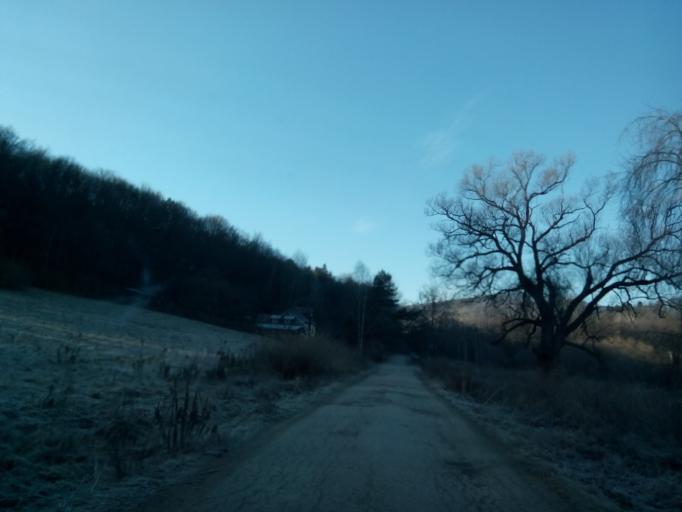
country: SK
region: Kosicky
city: Medzev
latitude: 48.6899
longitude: 20.9168
